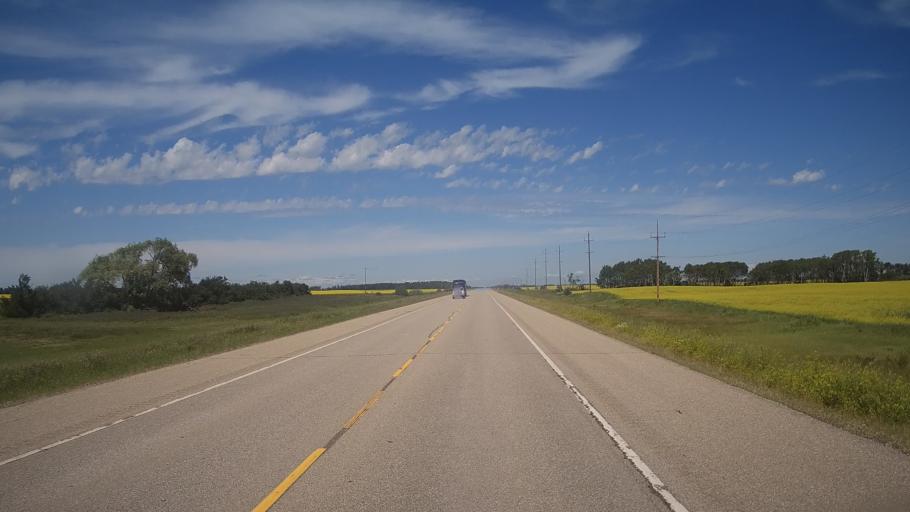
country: CA
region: Saskatchewan
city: Langenburg
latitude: 50.6649
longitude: -101.2761
